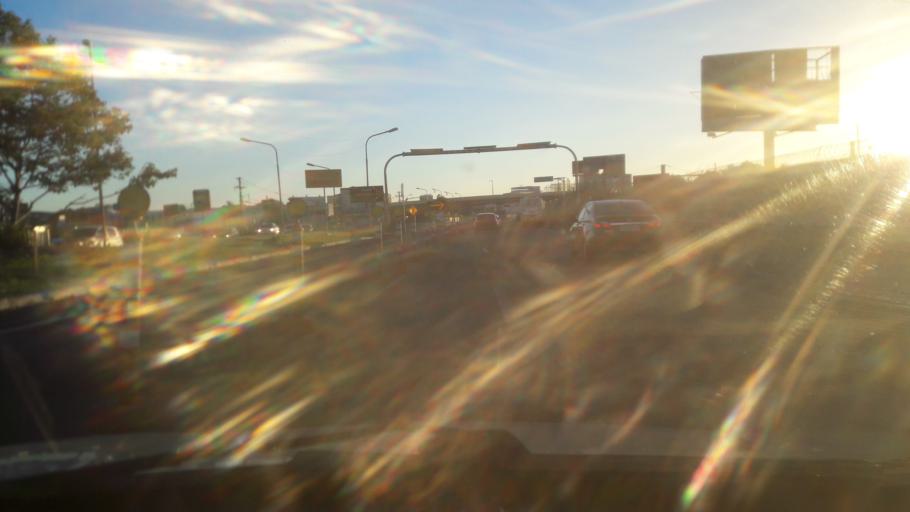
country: BR
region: Rio Grande do Sul
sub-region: Porto Alegre
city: Porto Alegre
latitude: -29.9942
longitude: -51.1878
